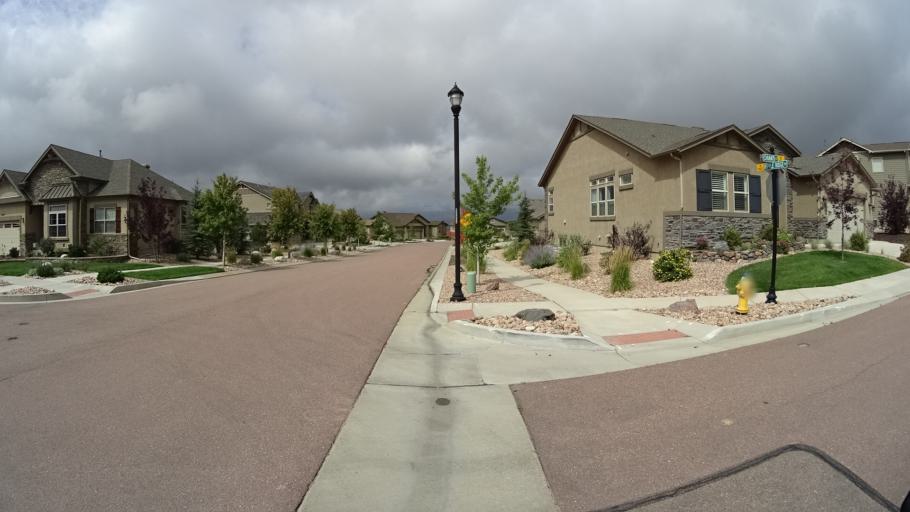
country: US
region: Colorado
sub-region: El Paso County
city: Gleneagle
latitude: 39.0143
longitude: -104.7870
